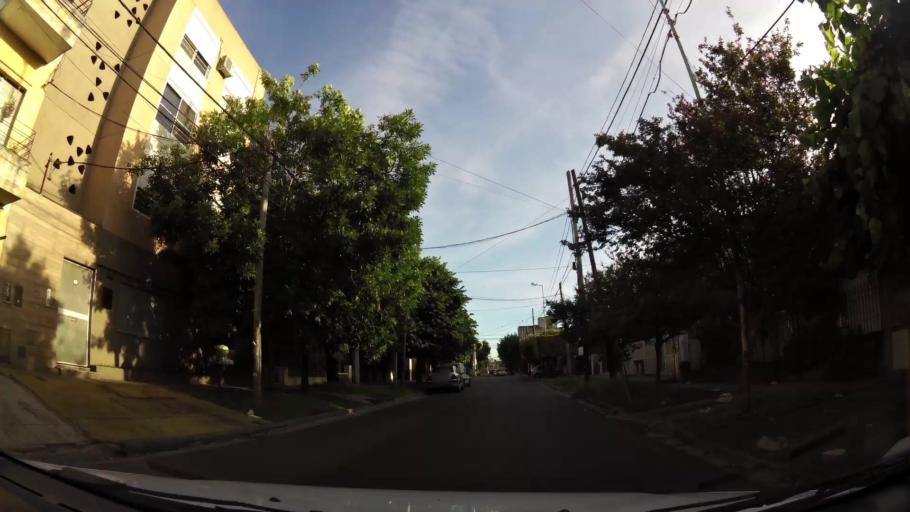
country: AR
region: Buenos Aires
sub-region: Partido de Moron
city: Moron
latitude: -34.6465
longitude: -58.6253
